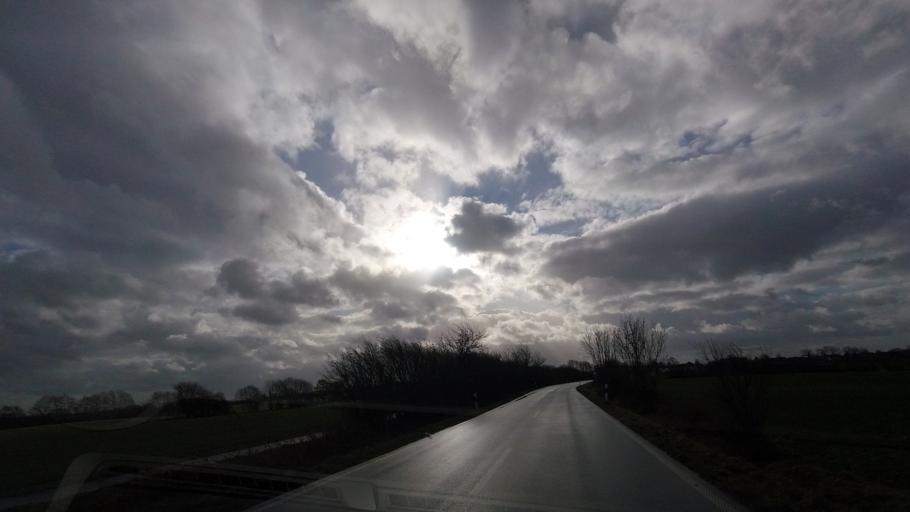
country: DE
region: Schleswig-Holstein
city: Grodersby
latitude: 54.6444
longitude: 9.9201
